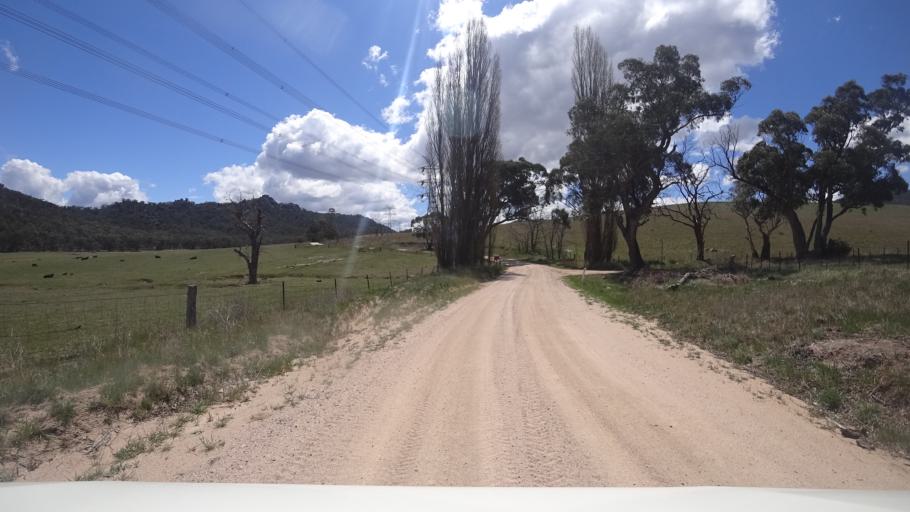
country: AU
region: New South Wales
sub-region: Oberon
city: Oberon
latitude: -33.5583
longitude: 149.9339
